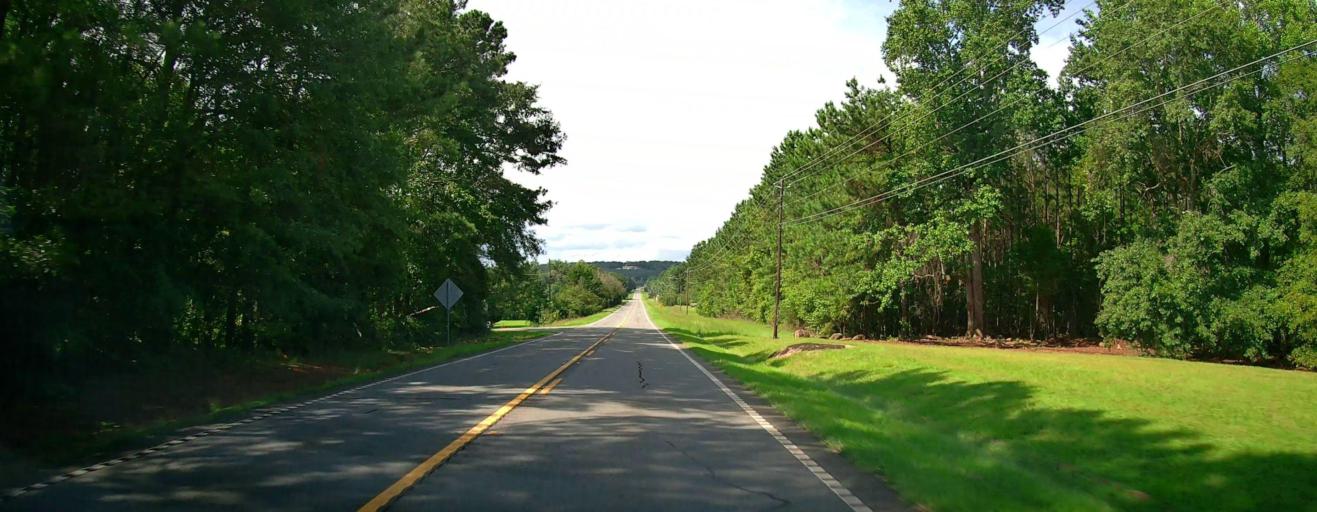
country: US
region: Georgia
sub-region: Meriwether County
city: Manchester
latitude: 32.8262
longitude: -84.6161
